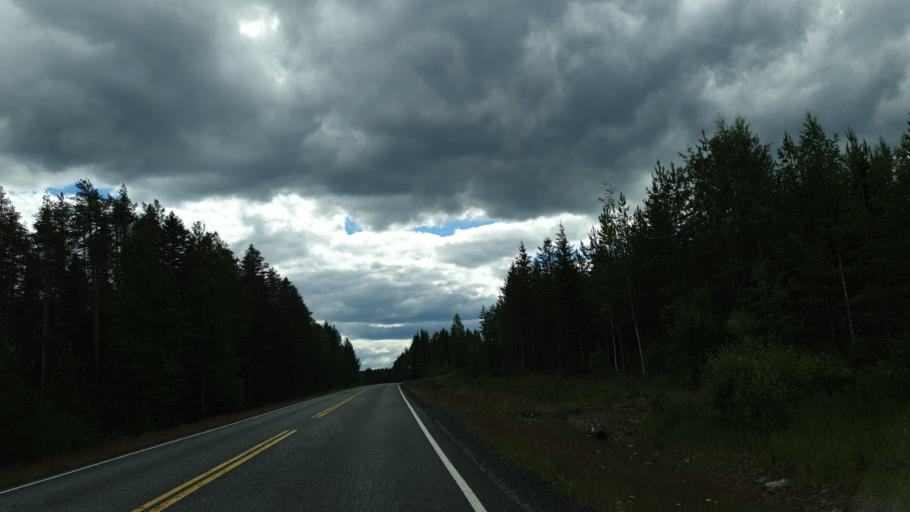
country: FI
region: Kainuu
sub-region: Kehys-Kainuu
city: Kuhmo
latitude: 63.9983
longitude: 29.6349
